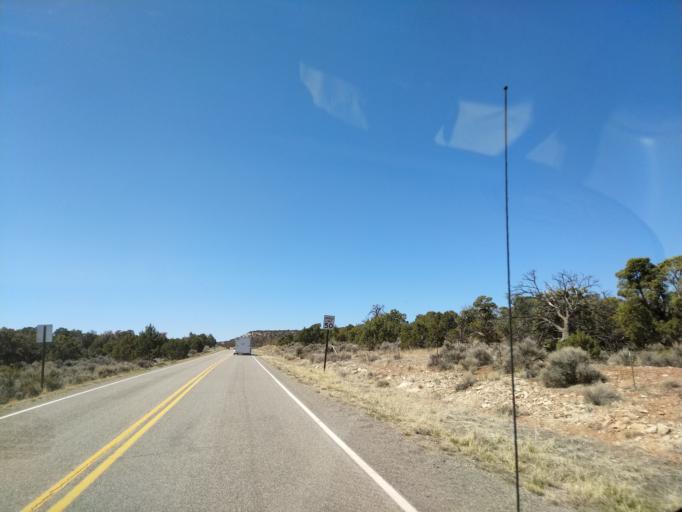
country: US
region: Colorado
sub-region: Mesa County
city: Redlands
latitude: 39.0177
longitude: -108.6622
